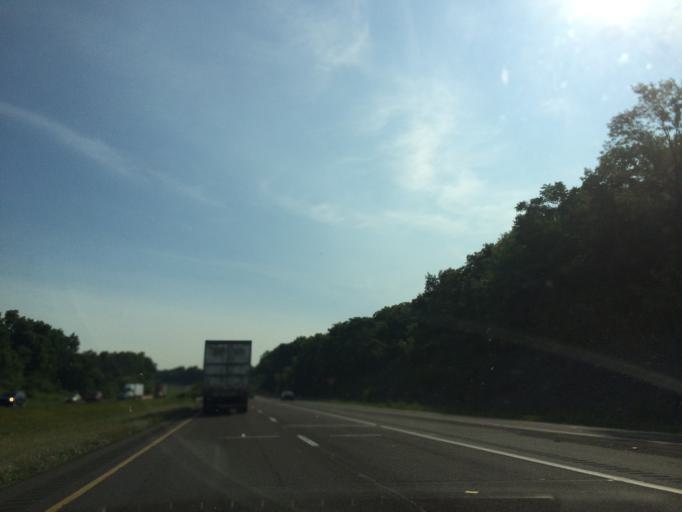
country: US
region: Pennsylvania
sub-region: Lancaster County
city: Brownstown
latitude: 40.1055
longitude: -76.2517
